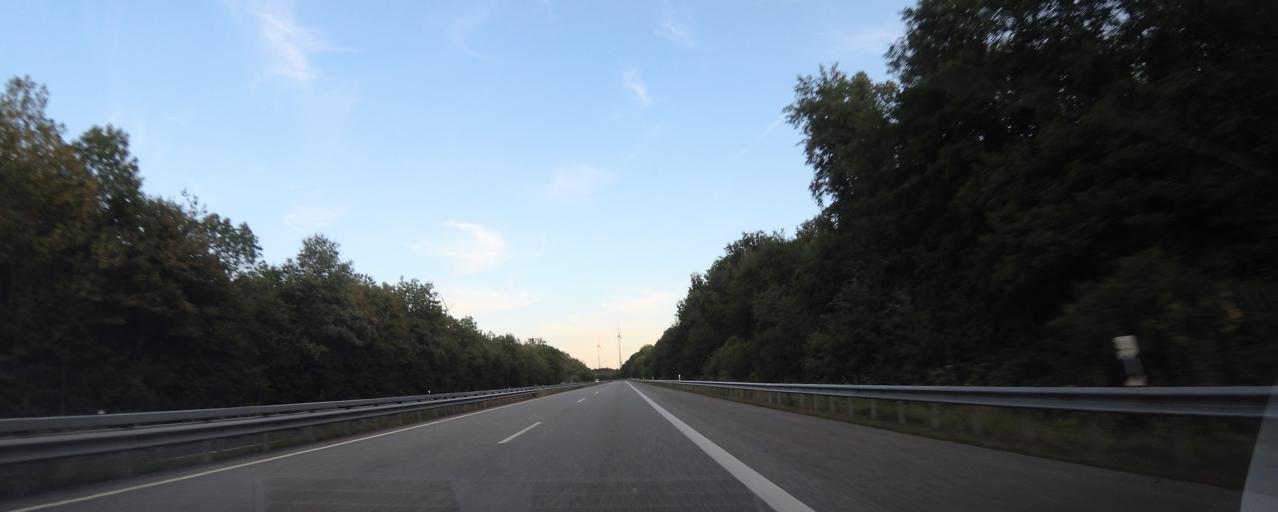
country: DE
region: Rheinland-Pfalz
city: Gimbweiler
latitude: 49.5963
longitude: 7.1917
